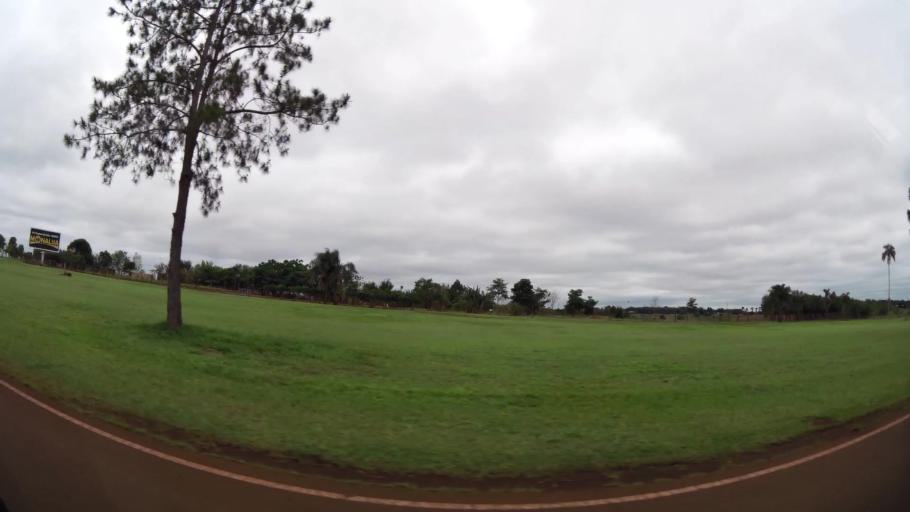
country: PY
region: Alto Parana
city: Colonia Yguazu
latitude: -25.4745
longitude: -54.8582
